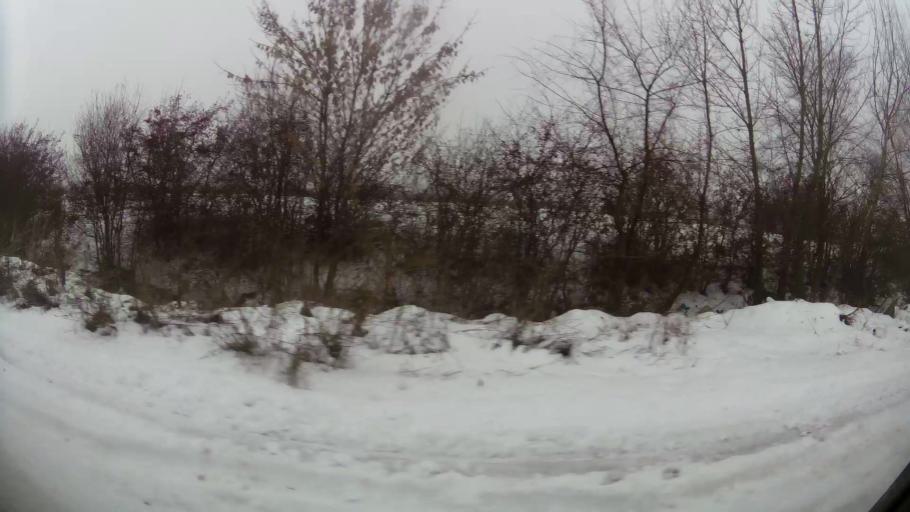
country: RO
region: Ilfov
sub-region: Comuna Chiajna
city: Chiajna
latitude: 44.4410
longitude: 25.9709
